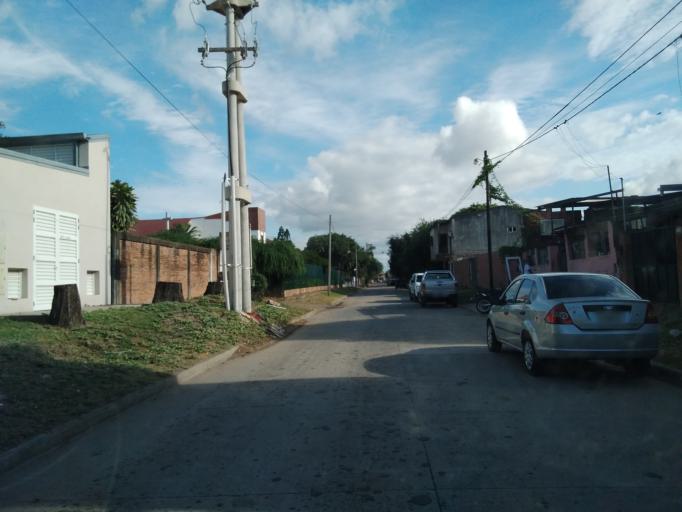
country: AR
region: Corrientes
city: Corrientes
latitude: -27.4642
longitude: -58.8124
